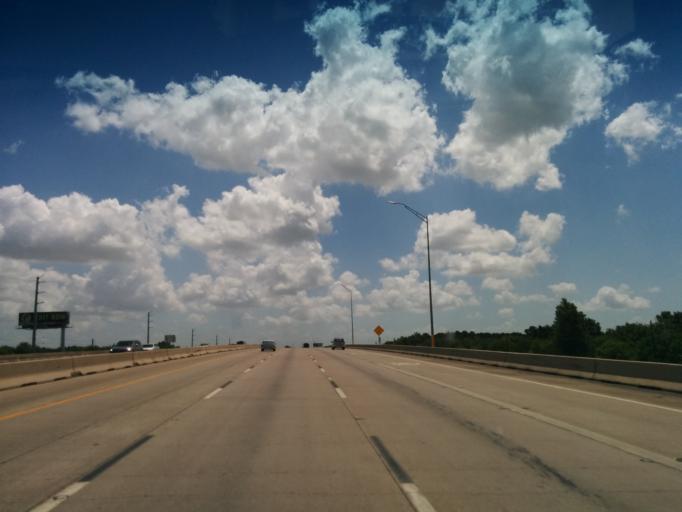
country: US
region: Texas
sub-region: Harris County
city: Highlands
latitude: 29.7998
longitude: -95.0198
